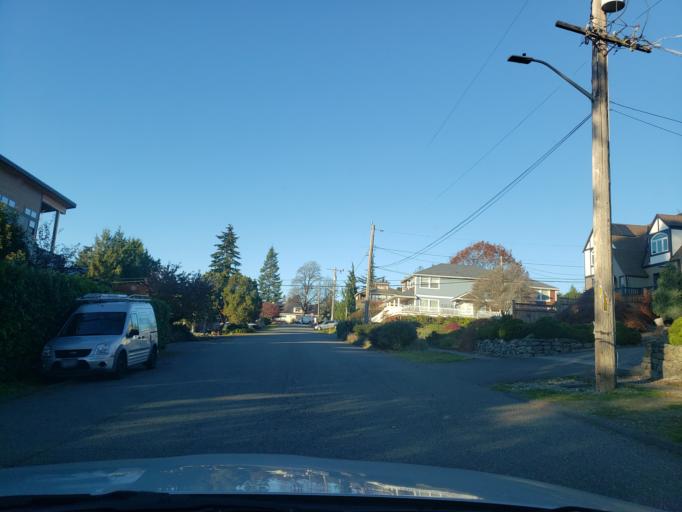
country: US
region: Washington
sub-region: Snohomish County
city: Woodway
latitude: 47.7721
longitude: -122.3885
